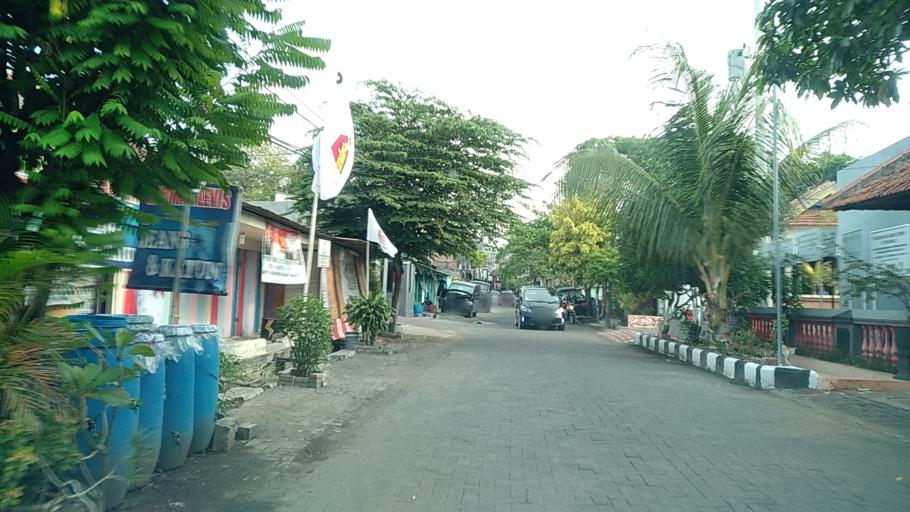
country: ID
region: Central Java
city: Semarang
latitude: -6.9864
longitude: 110.3803
